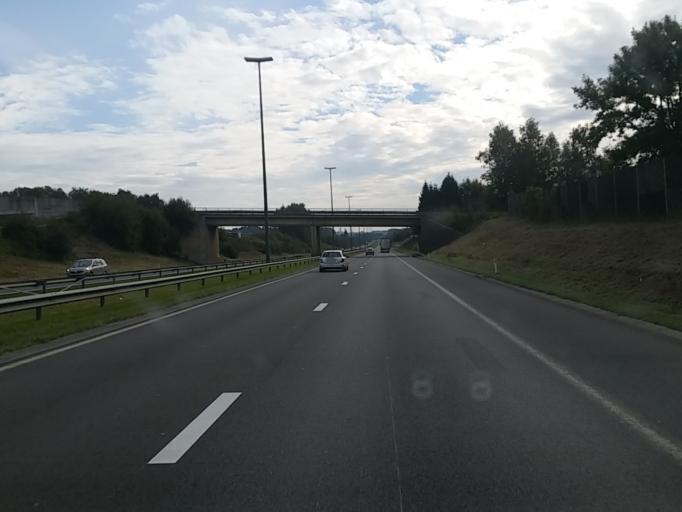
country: BE
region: Wallonia
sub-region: Province du Luxembourg
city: Attert
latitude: 49.6933
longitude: 5.7118
